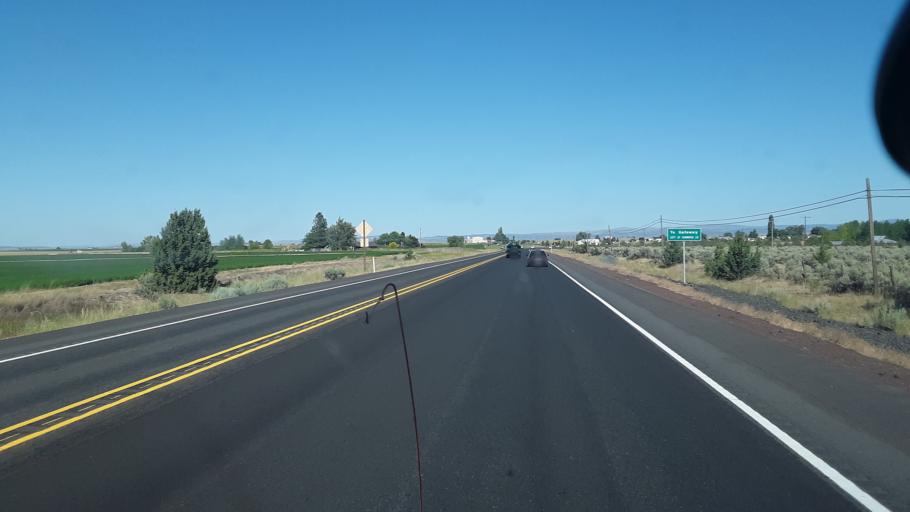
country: US
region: Oregon
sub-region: Jefferson County
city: Warm Springs
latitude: 44.7228
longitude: -121.1866
